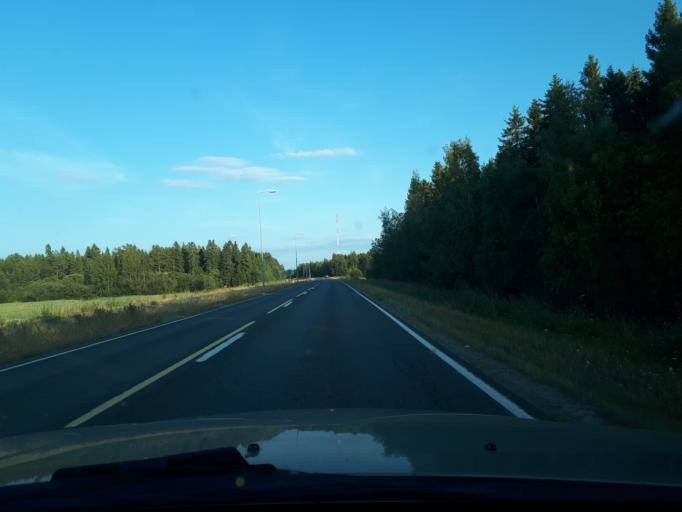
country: FI
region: Northern Ostrobothnia
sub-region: Oulu
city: Oulunsalo
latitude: 64.9779
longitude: 25.2795
